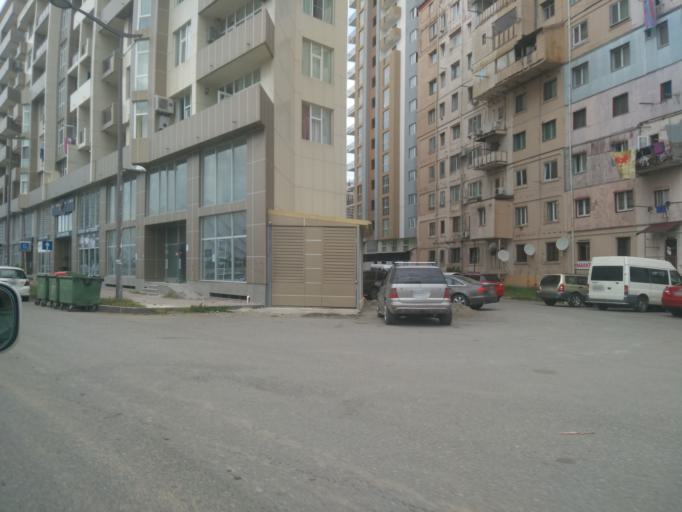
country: GE
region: Ajaria
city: Batumi
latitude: 41.6346
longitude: 41.6226
